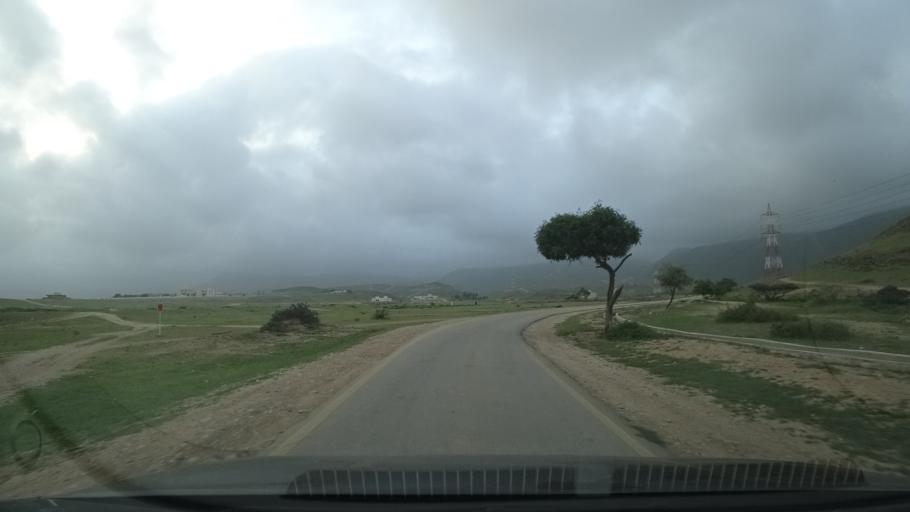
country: OM
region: Zufar
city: Salalah
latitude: 17.1130
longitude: 54.2269
